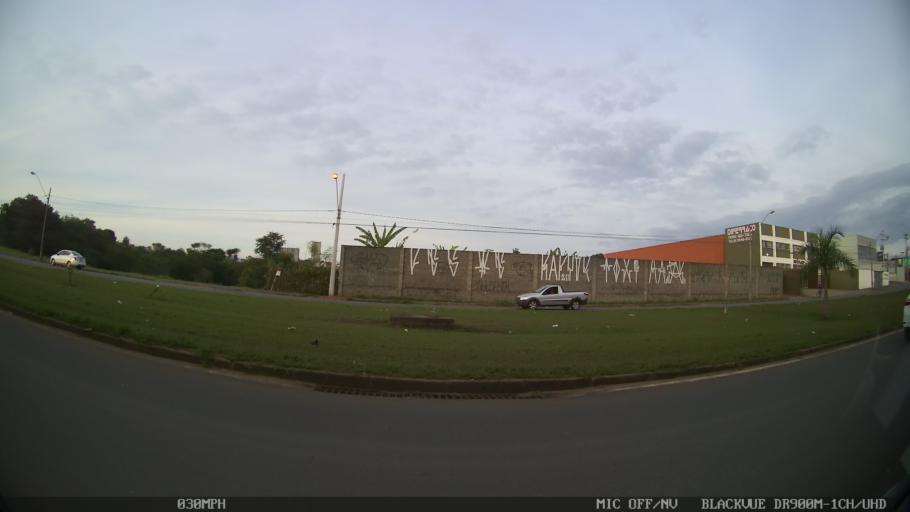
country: BR
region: Sao Paulo
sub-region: Limeira
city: Limeira
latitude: -22.5686
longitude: -47.3802
